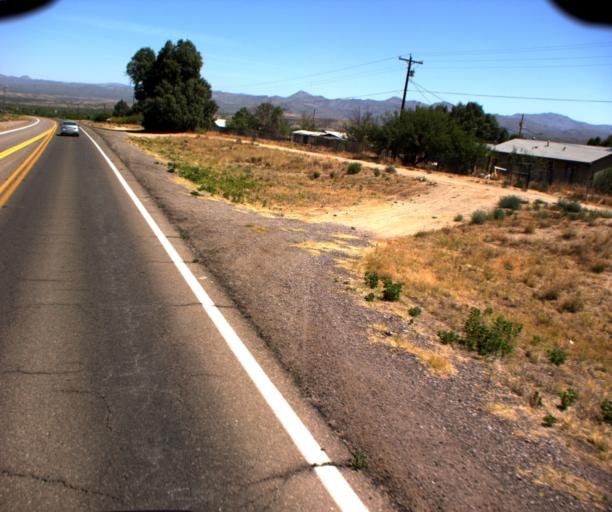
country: US
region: Arizona
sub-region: Graham County
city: Bylas
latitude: 33.1443
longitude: -110.1257
